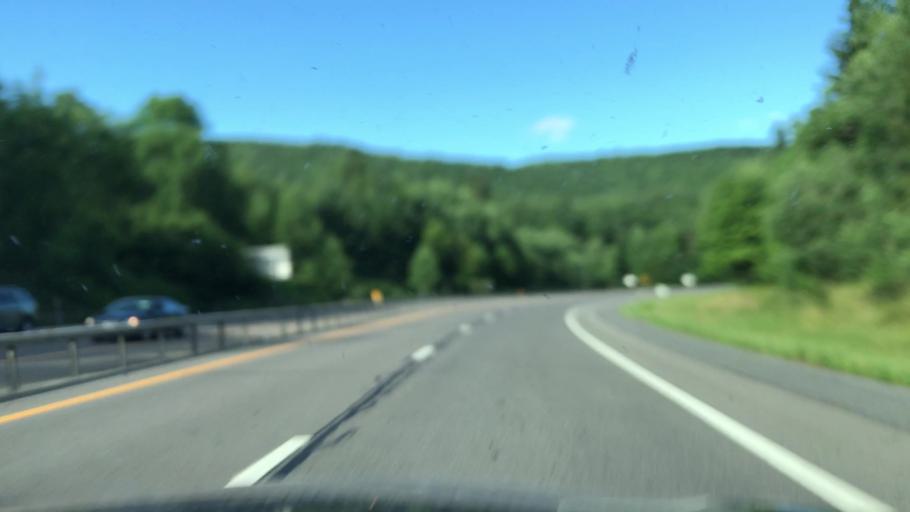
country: US
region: New York
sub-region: Delaware County
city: Hancock
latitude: 41.9595
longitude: -75.2850
